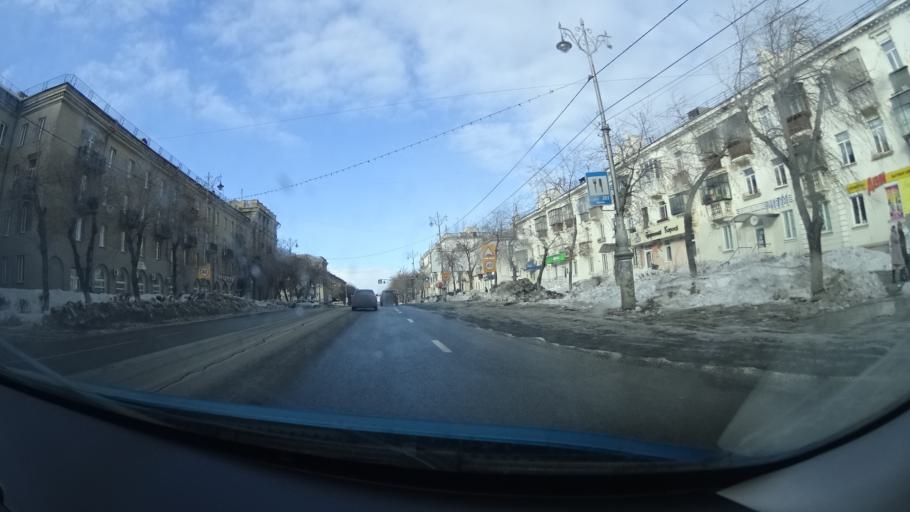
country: RU
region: Chelyabinsk
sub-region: Gorod Magnitogorsk
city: Magnitogorsk
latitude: 53.4288
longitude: 58.9837
